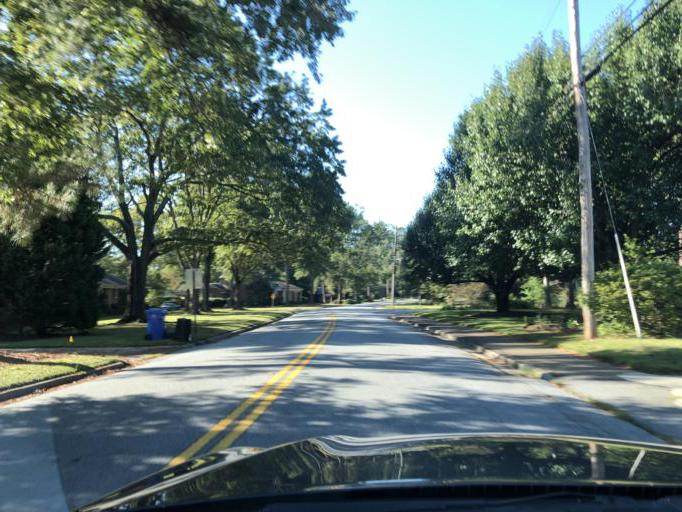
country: US
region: Georgia
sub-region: Muscogee County
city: Columbus
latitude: 32.4890
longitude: -84.9455
